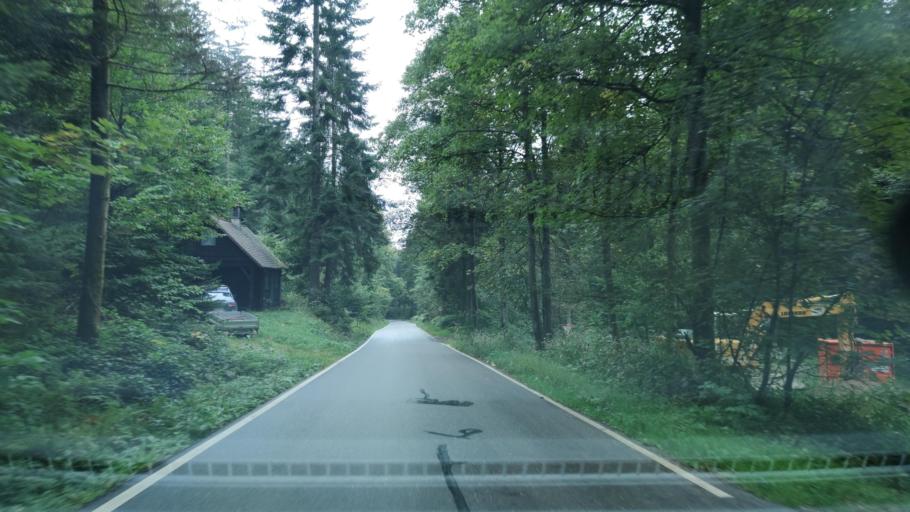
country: DE
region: Baden-Wuerttemberg
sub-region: Freiburg Region
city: Sasbachwalden
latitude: 48.6309
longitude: 8.1728
